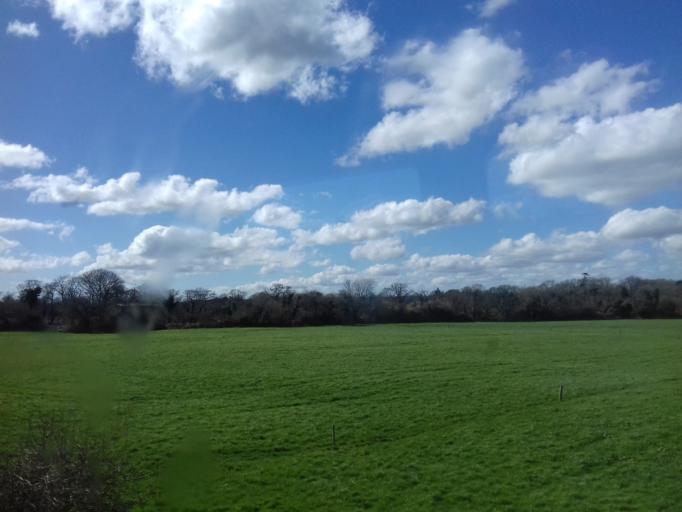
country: IE
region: Munster
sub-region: County Cork
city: Kanturk
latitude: 52.0979
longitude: -8.9686
